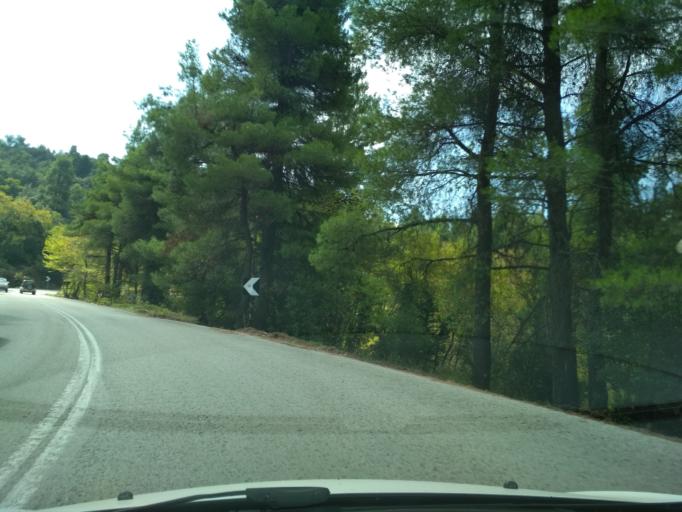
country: GR
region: Central Greece
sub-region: Nomos Evvoias
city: Politika
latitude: 38.6681
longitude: 23.5579
